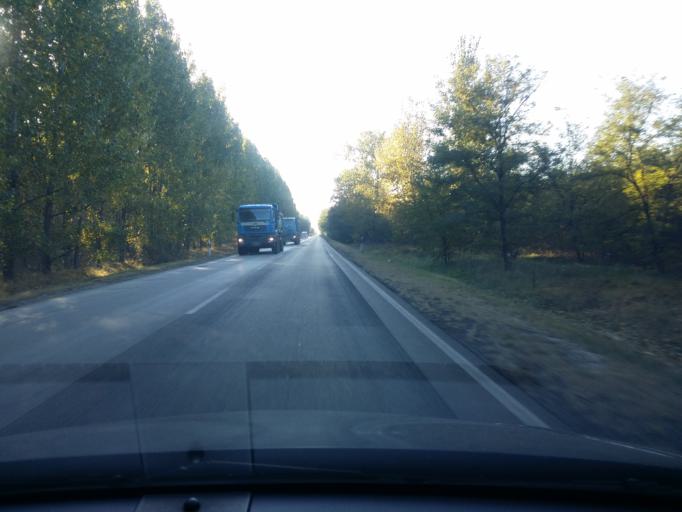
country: HU
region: Bacs-Kiskun
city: Nyarlorinc
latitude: 46.8881
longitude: 19.8357
